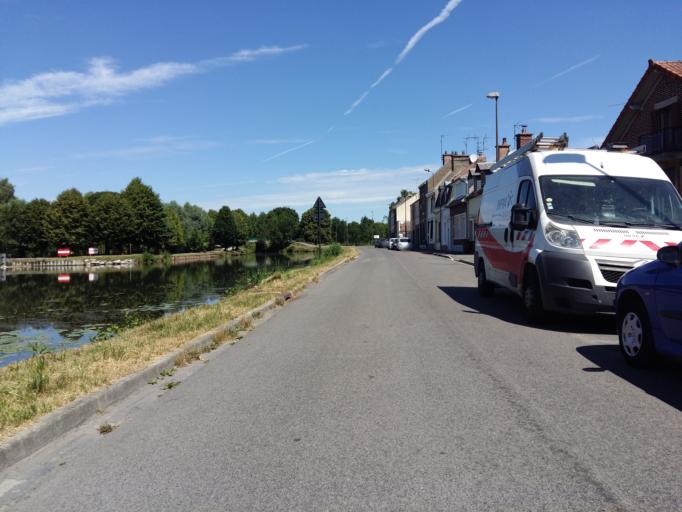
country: FR
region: Picardie
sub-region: Departement de la Somme
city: Amiens
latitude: 49.9074
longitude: 2.2821
